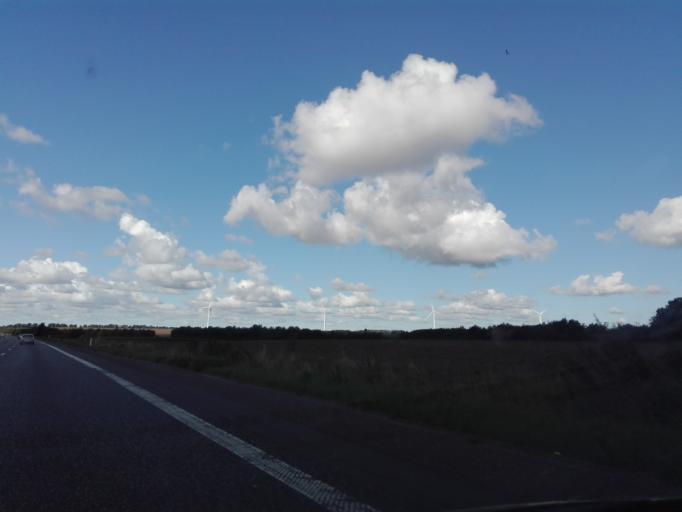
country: DK
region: Central Jutland
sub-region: Randers Kommune
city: Spentrup
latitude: 56.5143
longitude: 9.9656
